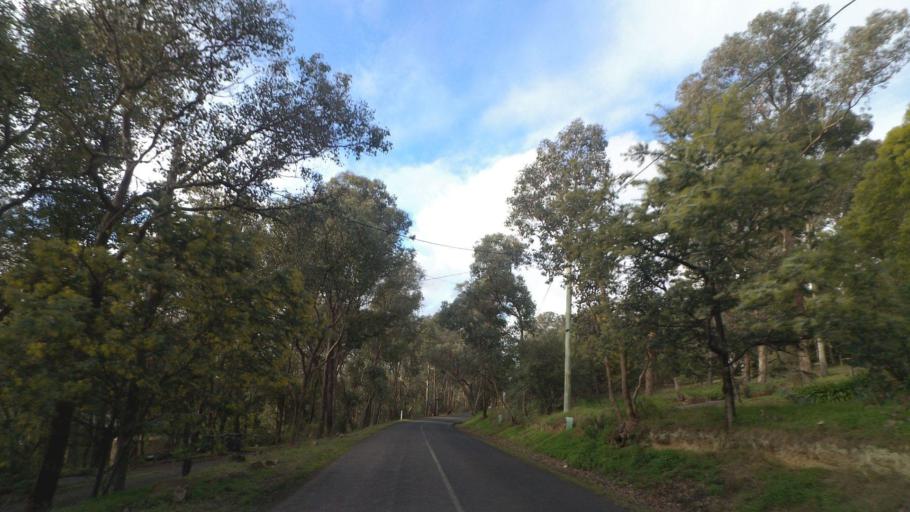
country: AU
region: Victoria
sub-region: Nillumbik
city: North Warrandyte
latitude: -37.7387
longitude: 145.2087
